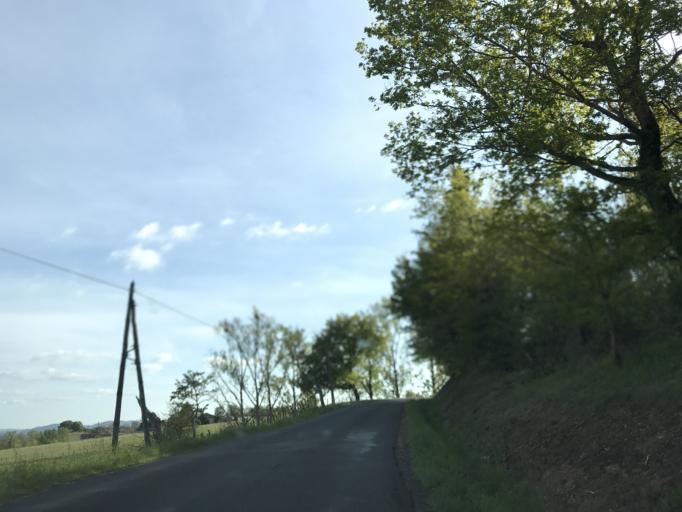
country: FR
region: Auvergne
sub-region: Departement du Puy-de-Dome
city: Courpiere
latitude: 45.7341
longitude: 3.4810
